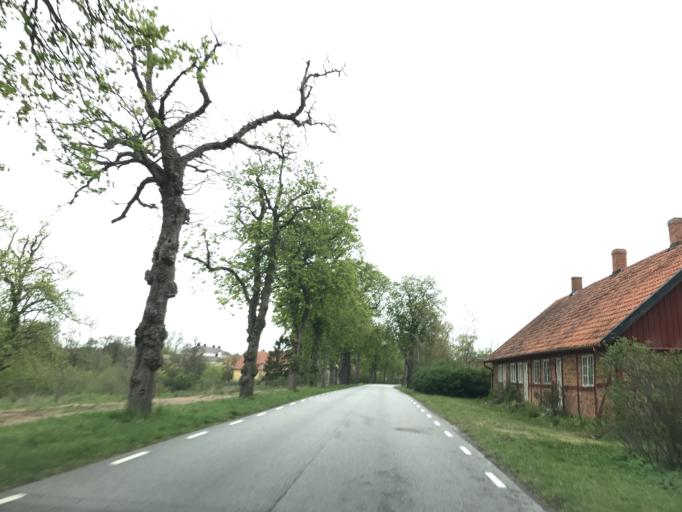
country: SE
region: Skane
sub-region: Trelleborgs Kommun
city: Anderslov
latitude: 55.5044
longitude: 13.3290
